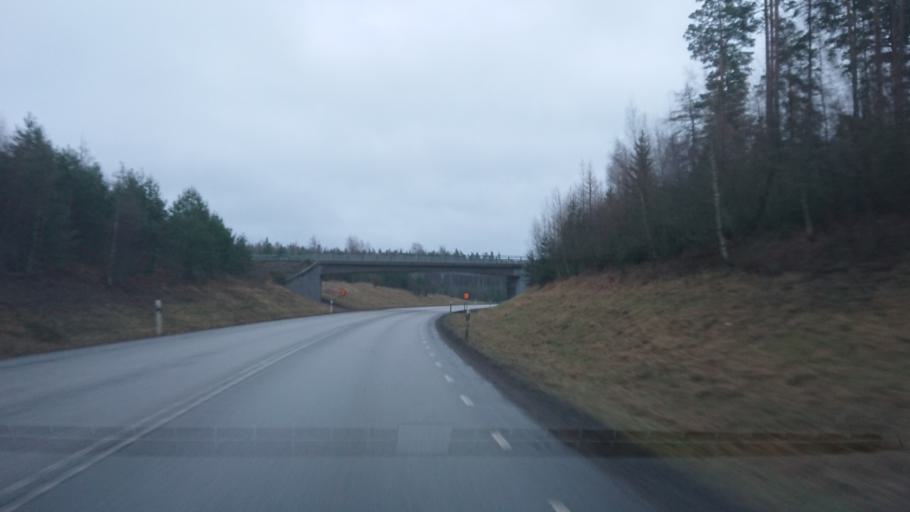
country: SE
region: Uppsala
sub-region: Osthammars Kommun
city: Bjorklinge
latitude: 60.0187
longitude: 17.5814
